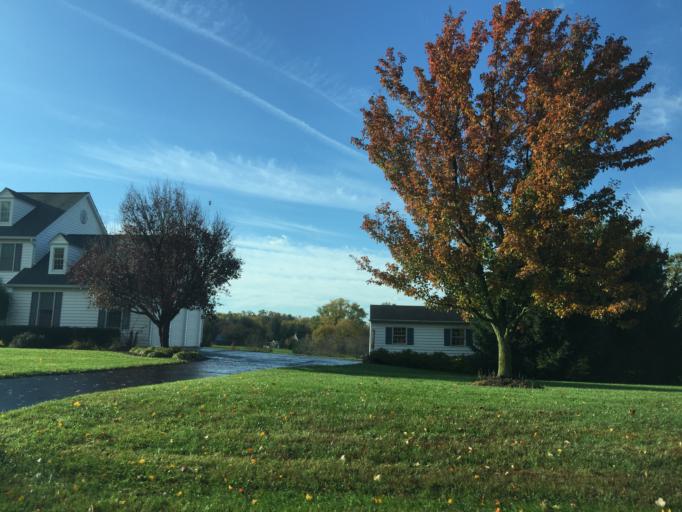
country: US
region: Maryland
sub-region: Howard County
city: Highland
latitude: 39.2690
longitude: -77.0099
